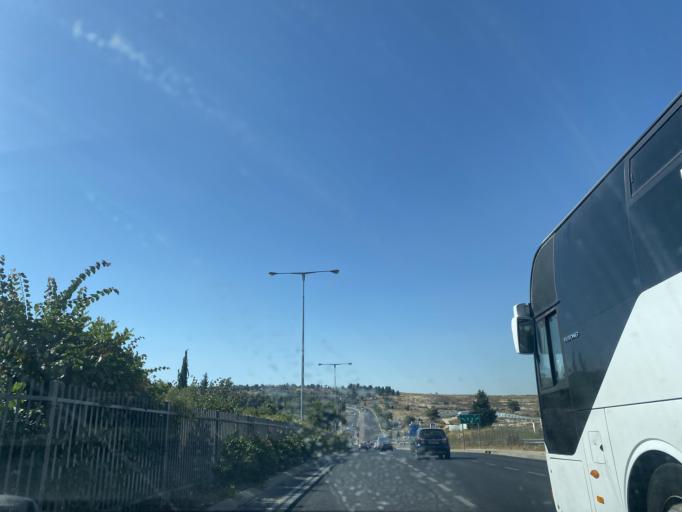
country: PS
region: West Bank
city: Bayt Iksa
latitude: 31.8240
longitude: 35.1891
